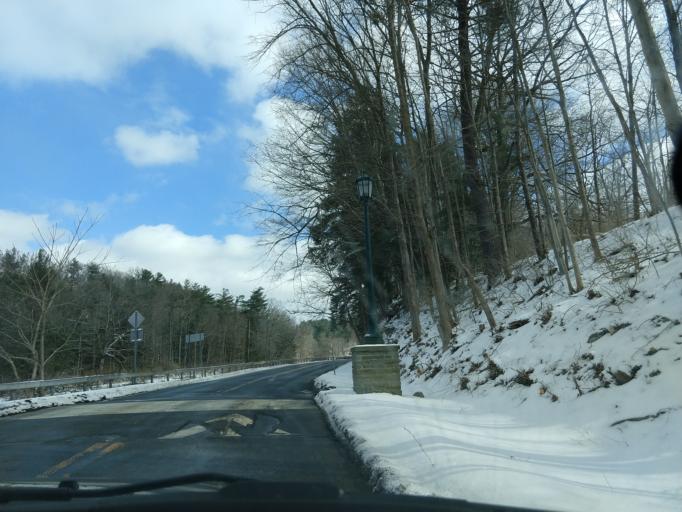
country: US
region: New York
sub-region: Tompkins County
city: Northeast Ithaca
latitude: 42.4530
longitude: -76.4621
